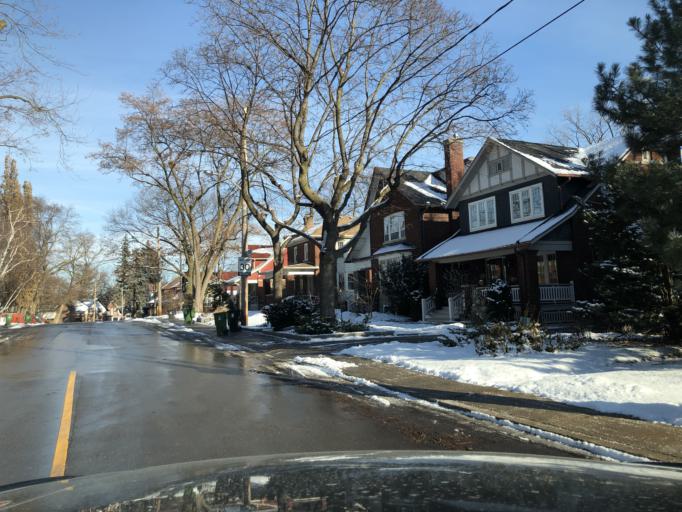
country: CA
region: Ontario
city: Etobicoke
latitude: 43.7025
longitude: -79.5156
